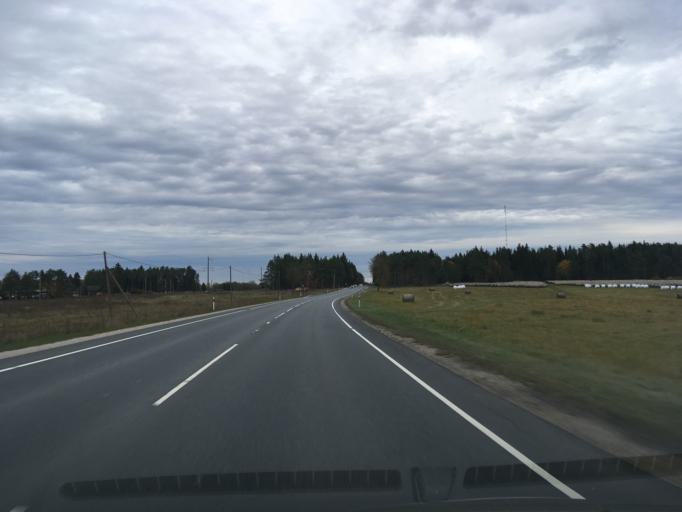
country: EE
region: Harju
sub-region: Nissi vald
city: Turba
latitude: 59.0272
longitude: 24.1511
